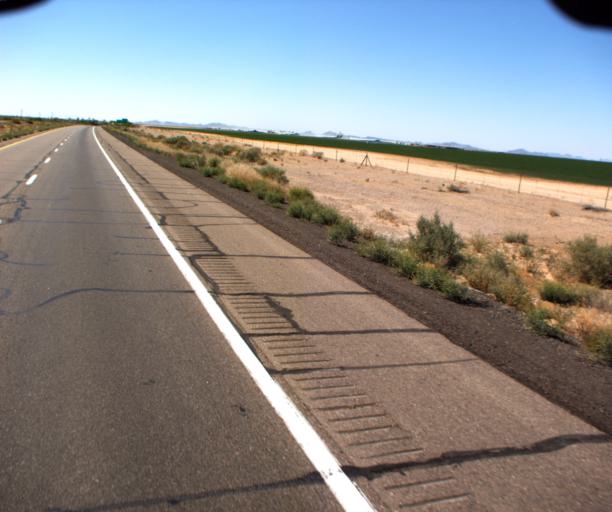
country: US
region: Arizona
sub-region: Maricopa County
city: Gila Bend
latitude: 32.9346
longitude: -112.7862
